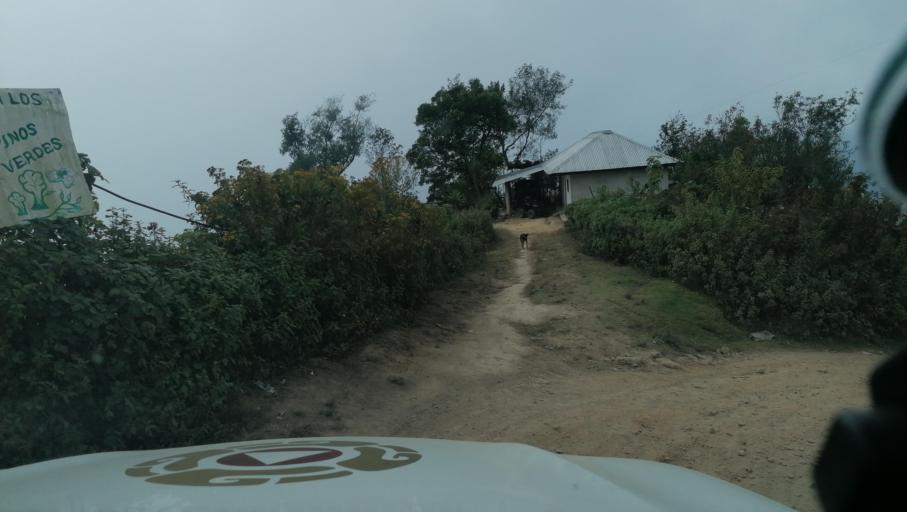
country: GT
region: San Marcos
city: Tacana
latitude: 15.2190
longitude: -92.1885
